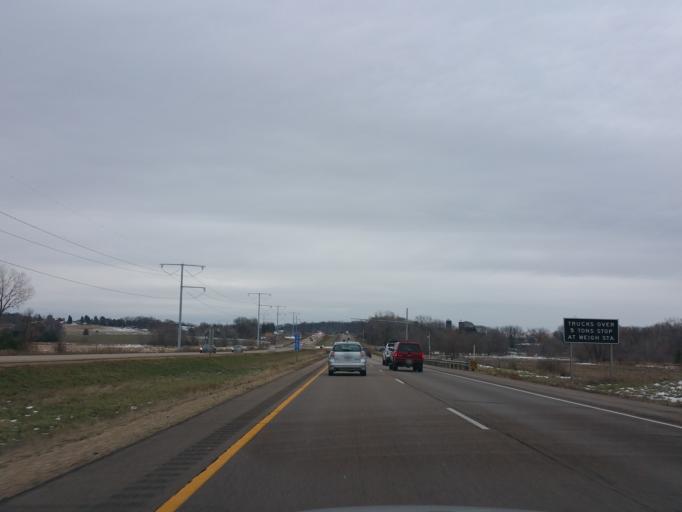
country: US
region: Wisconsin
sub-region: Dane County
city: McFarland
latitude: 43.0169
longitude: -89.2404
